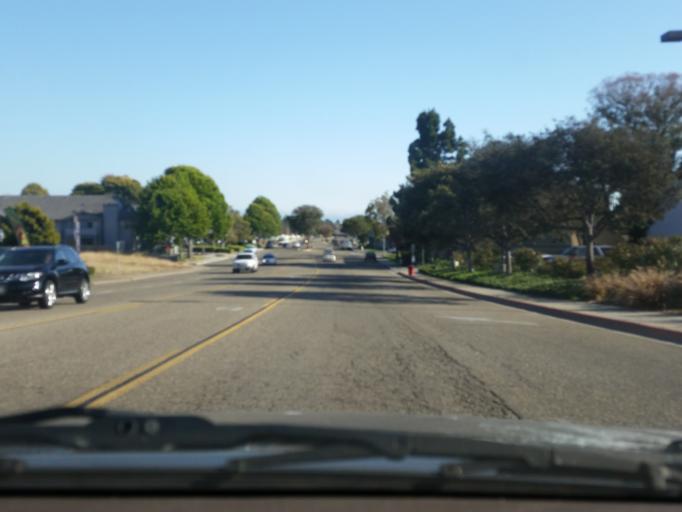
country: US
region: California
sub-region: San Luis Obispo County
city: Grover Beach
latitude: 35.1203
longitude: -120.6093
